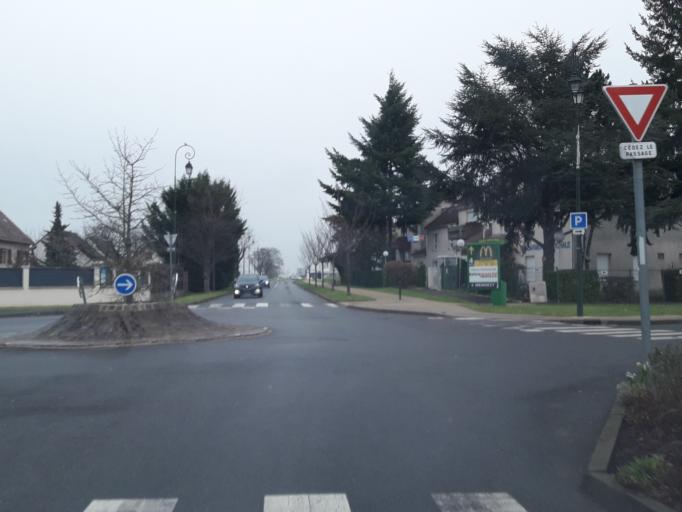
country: FR
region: Ile-de-France
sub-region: Departement de l'Essonne
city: Ballancourt-sur-Essonne
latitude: 48.5289
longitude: 2.3862
